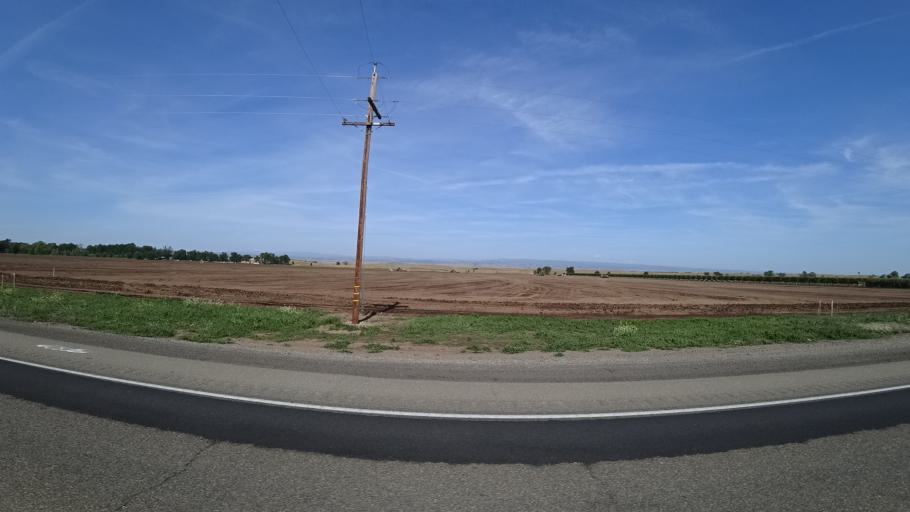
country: US
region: California
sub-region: Tehama County
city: Los Molinos
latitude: 39.9702
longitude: -122.0739
